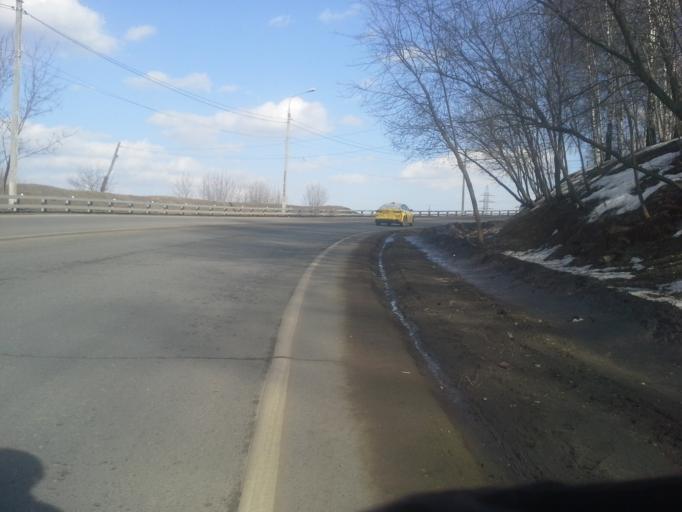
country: RU
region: Moskovskaya
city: Shcherbinka
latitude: 55.4886
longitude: 37.5111
